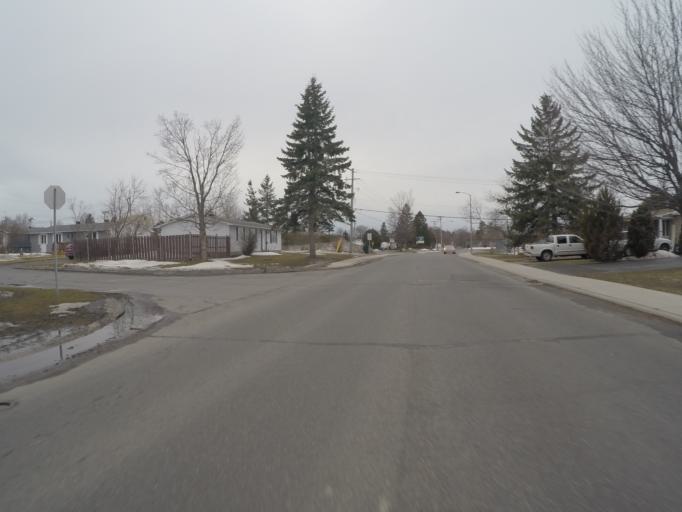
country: CA
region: Quebec
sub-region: Outaouais
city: Gatineau
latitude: 45.4720
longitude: -75.5070
